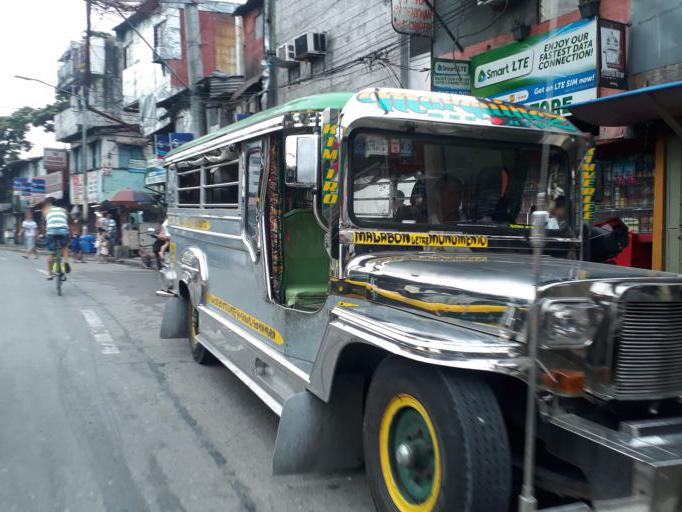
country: PH
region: Metro Manila
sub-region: Caloocan City
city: Niugan
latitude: 14.6573
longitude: 120.9743
